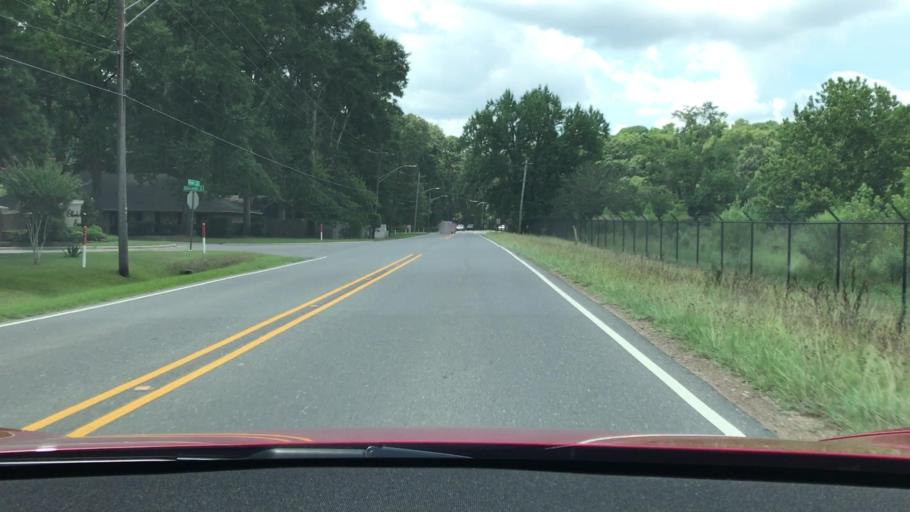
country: US
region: Louisiana
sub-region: Bossier Parish
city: Bossier City
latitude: 32.3901
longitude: -93.7219
